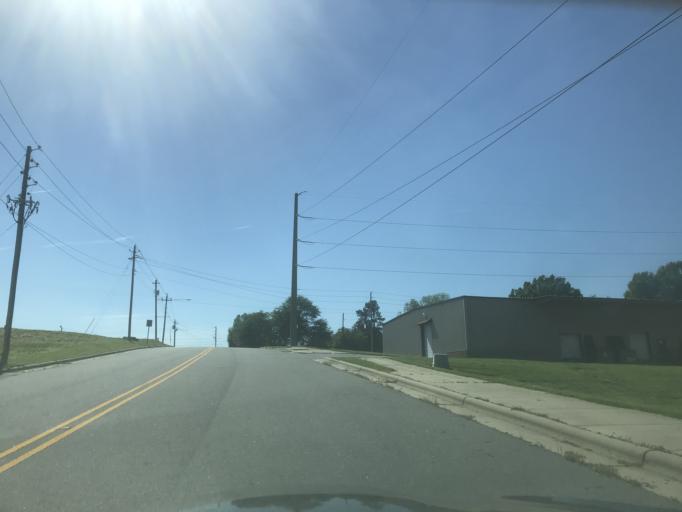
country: US
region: North Carolina
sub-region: Wake County
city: Raleigh
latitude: 35.7581
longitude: -78.6467
